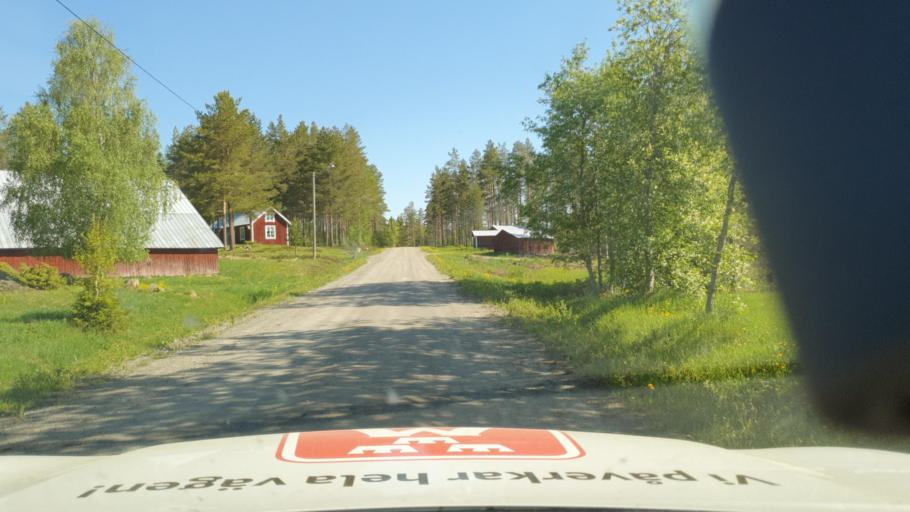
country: SE
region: Vaesterbotten
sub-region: Vannas Kommun
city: Vannasby
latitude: 63.9941
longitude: 19.7874
